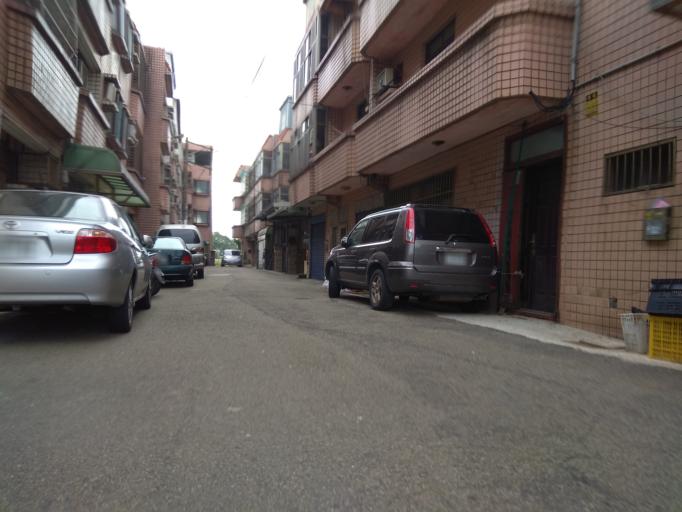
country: TW
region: Taiwan
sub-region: Hsinchu
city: Zhubei
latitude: 24.9840
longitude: 121.0522
